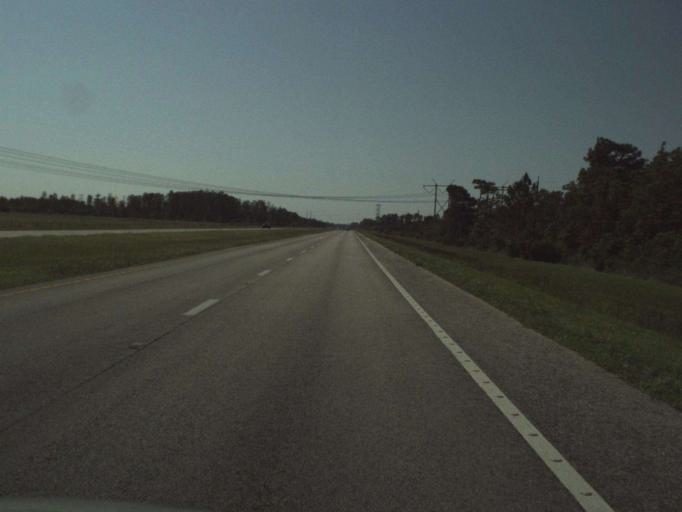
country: US
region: Florida
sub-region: Orange County
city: Wedgefield
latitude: 28.5120
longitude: -81.0607
